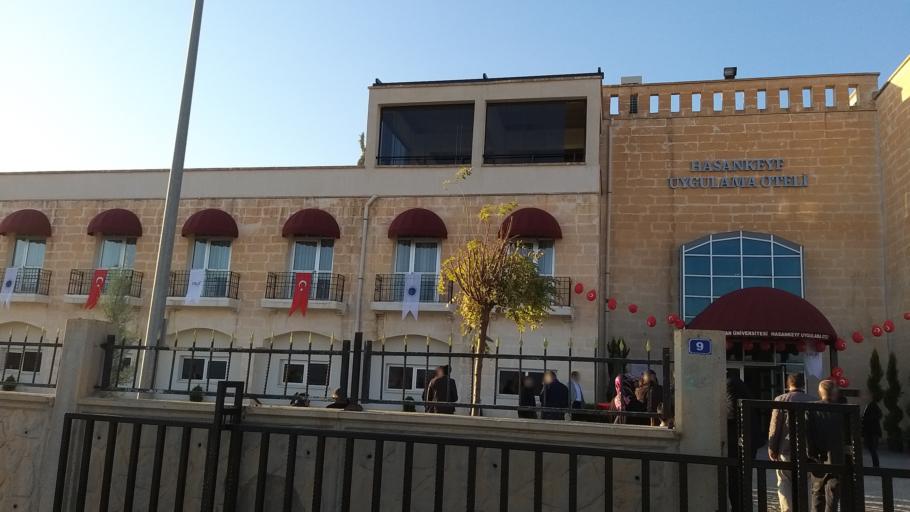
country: TR
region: Batman
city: Hasankeyf
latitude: 37.7307
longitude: 41.4230
